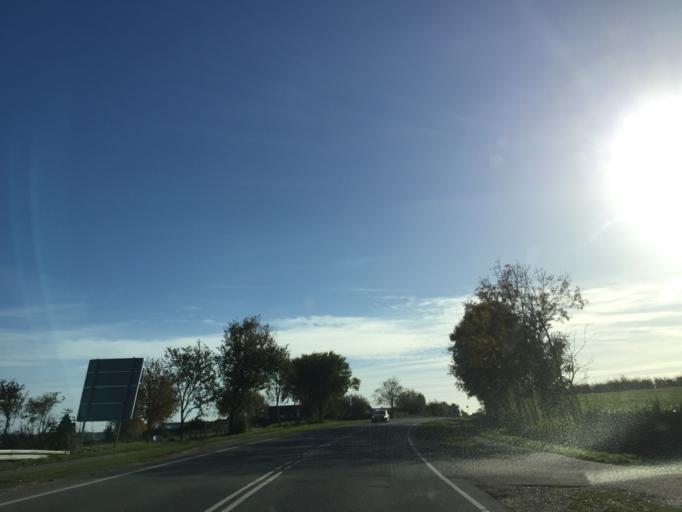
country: DK
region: South Denmark
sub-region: Sonderborg Kommune
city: Dybbol
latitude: 54.9194
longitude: 9.7562
